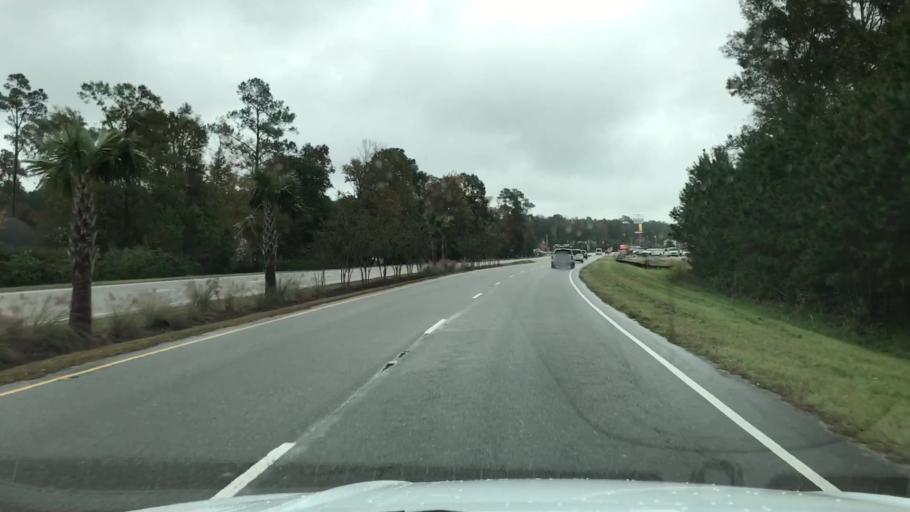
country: US
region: South Carolina
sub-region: Horry County
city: Myrtle Beach
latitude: 33.7583
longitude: -78.8635
